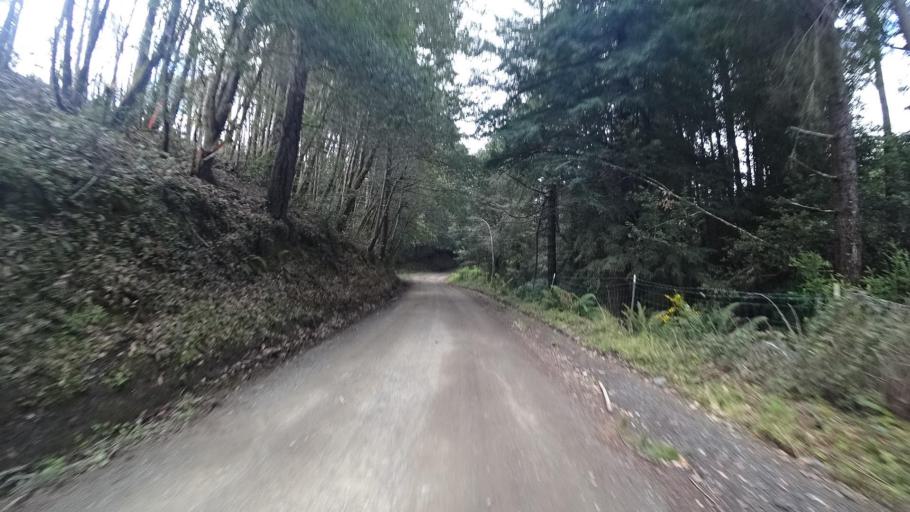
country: US
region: California
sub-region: Humboldt County
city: Blue Lake
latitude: 40.7686
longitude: -123.9555
